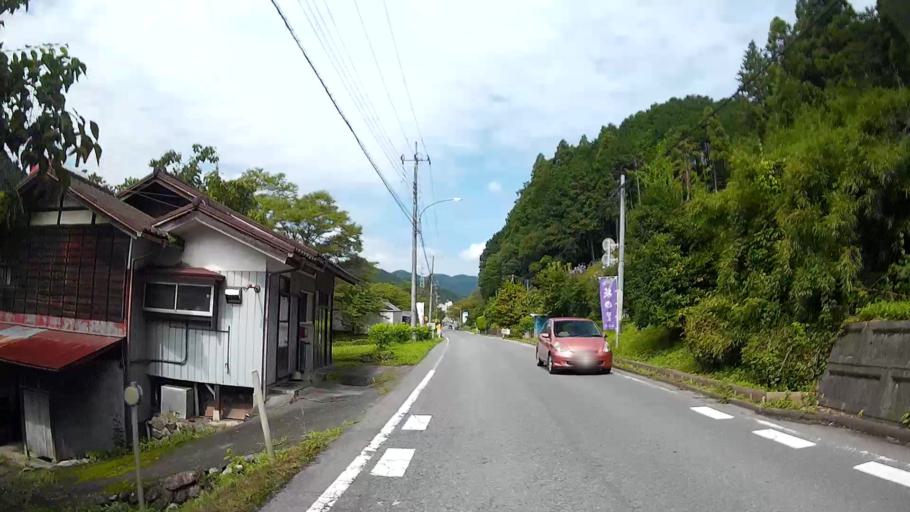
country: JP
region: Saitama
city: Hanno
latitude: 35.8672
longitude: 139.2537
